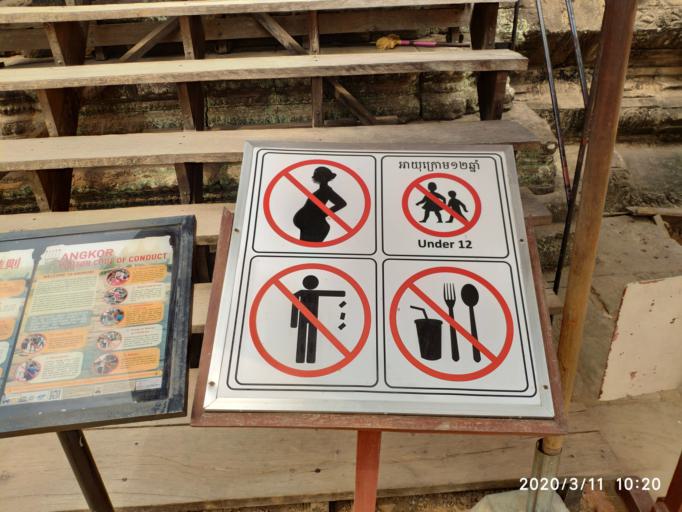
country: KH
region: Siem Reap
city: Siem Reap
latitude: 13.4438
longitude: 103.8569
